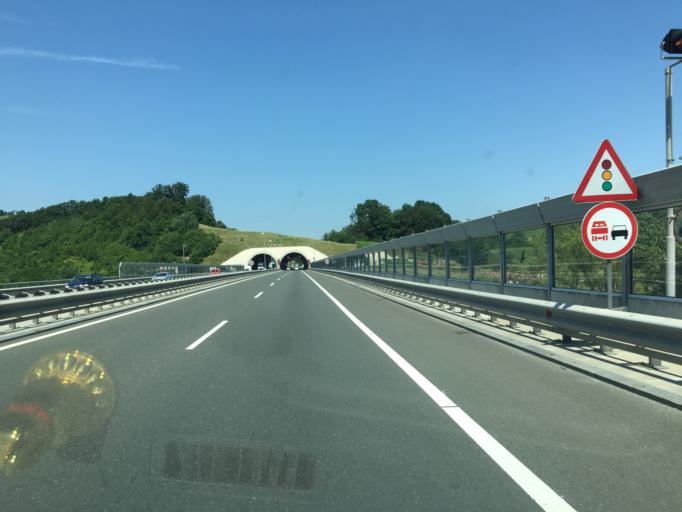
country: SI
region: Maribor
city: Maribor
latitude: 46.5552
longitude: 15.6899
